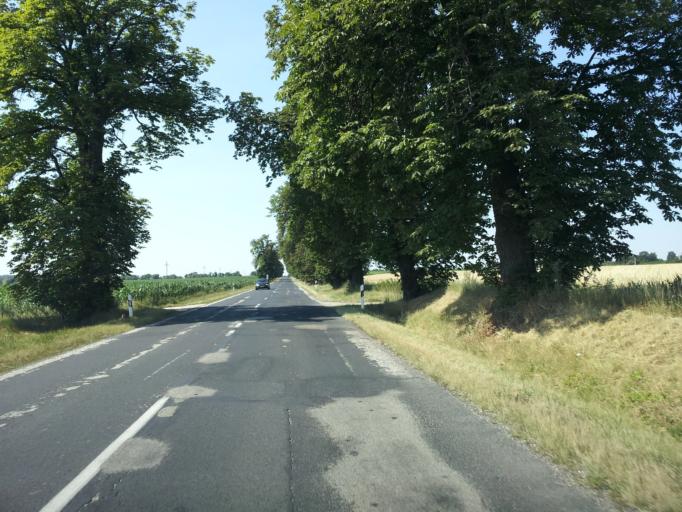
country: HU
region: Fejer
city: Lovasbereny
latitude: 47.2936
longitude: 18.5334
